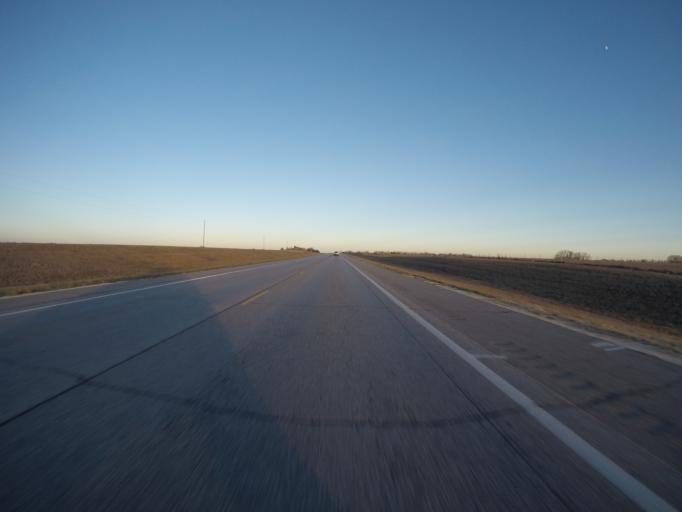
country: US
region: Kansas
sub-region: Marion County
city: Peabody
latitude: 38.1747
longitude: -97.1712
